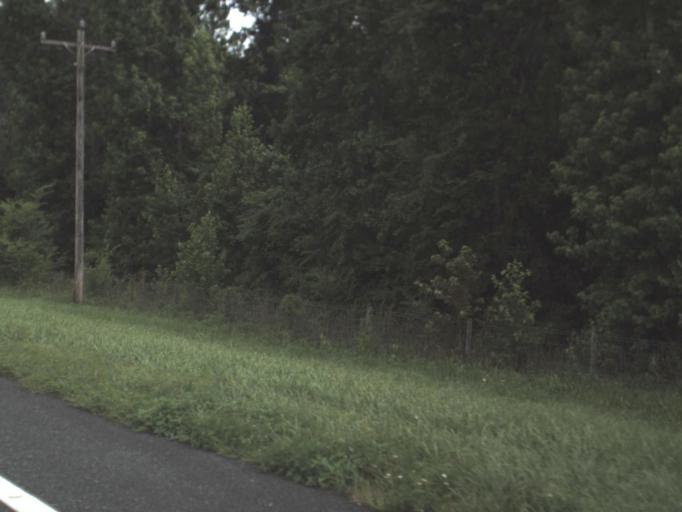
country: US
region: Florida
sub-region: Levy County
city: Williston
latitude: 29.3656
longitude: -82.4090
